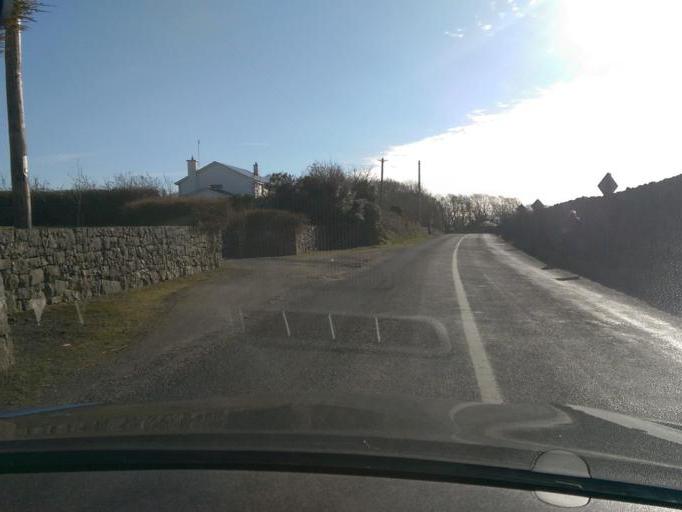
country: IE
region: Connaught
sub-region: County Galway
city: Oranmore
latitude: 53.2538
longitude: -8.9377
